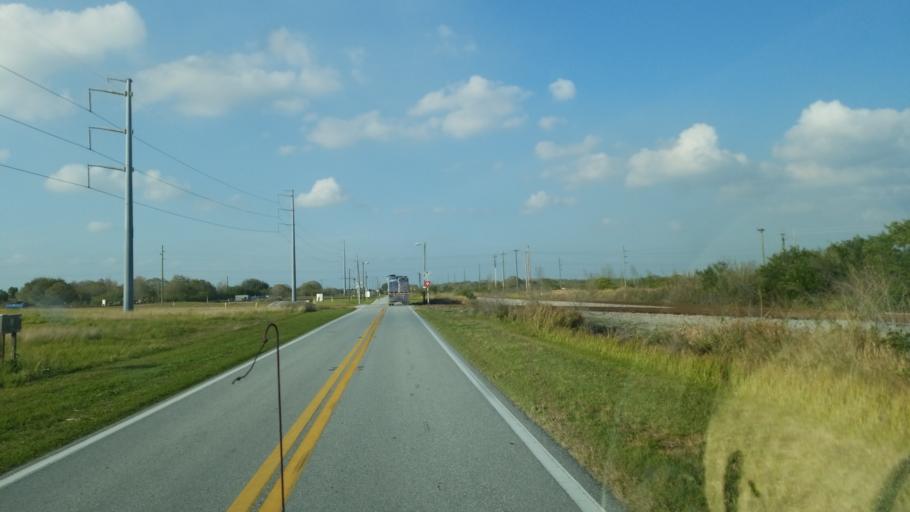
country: US
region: Florida
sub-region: Hardee County
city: Bowling Green
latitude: 27.6832
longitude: -81.9555
